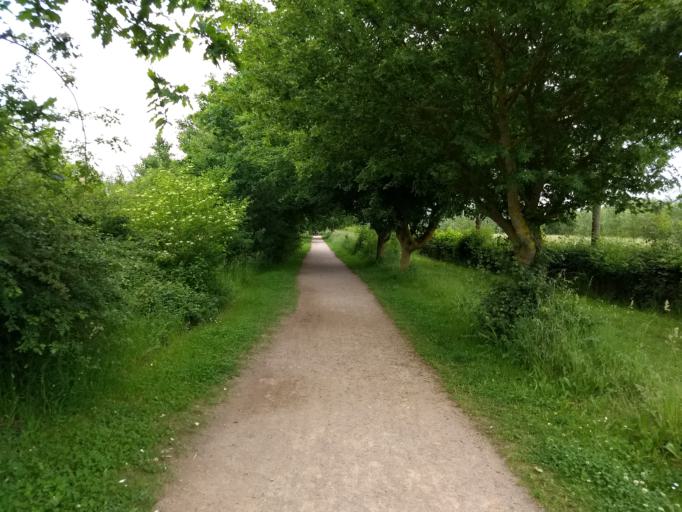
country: GB
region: England
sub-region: Central Bedfordshire
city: Marston Moretaine
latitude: 52.0634
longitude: -0.5392
